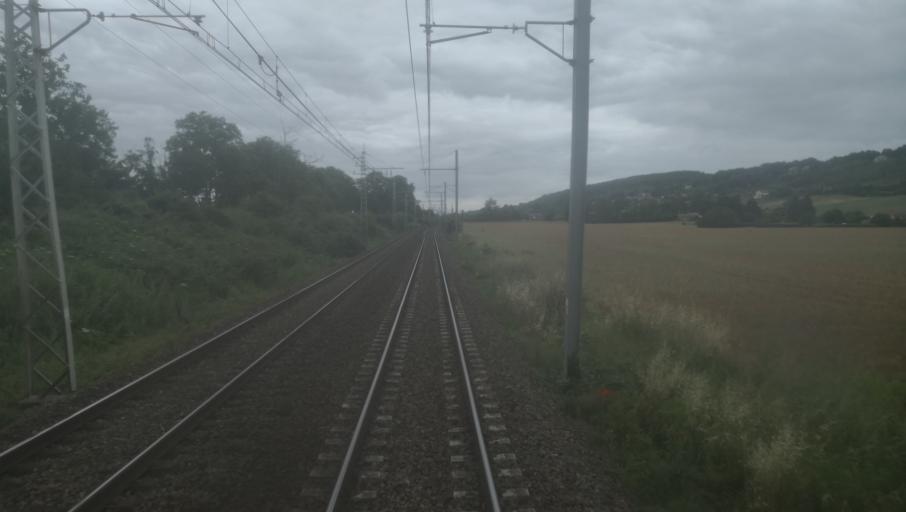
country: FR
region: Midi-Pyrenees
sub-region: Departement de la Haute-Garonne
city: Castelnau-d'Estretefonds
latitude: 43.7946
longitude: 1.3335
